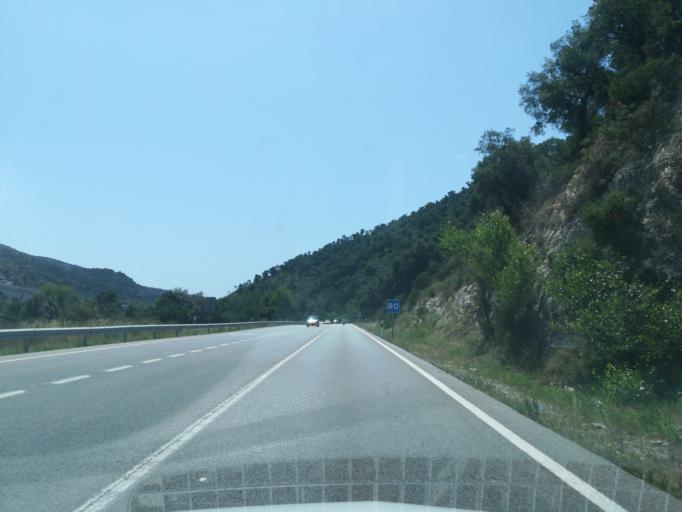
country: ES
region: Catalonia
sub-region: Provincia de Girona
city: la Jonquera
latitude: 42.4551
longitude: 2.8650
